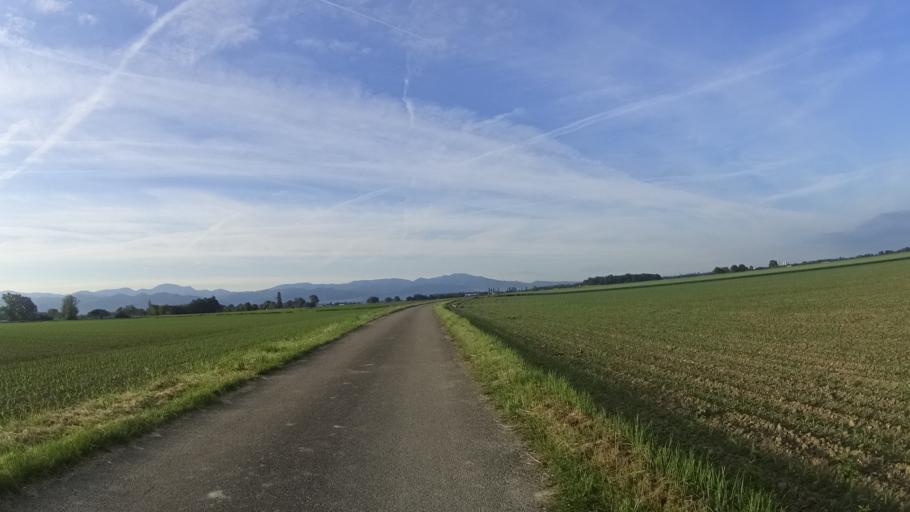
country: DE
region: Baden-Wuerttemberg
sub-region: Freiburg Region
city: Hartheim
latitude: 47.9623
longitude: 7.6438
